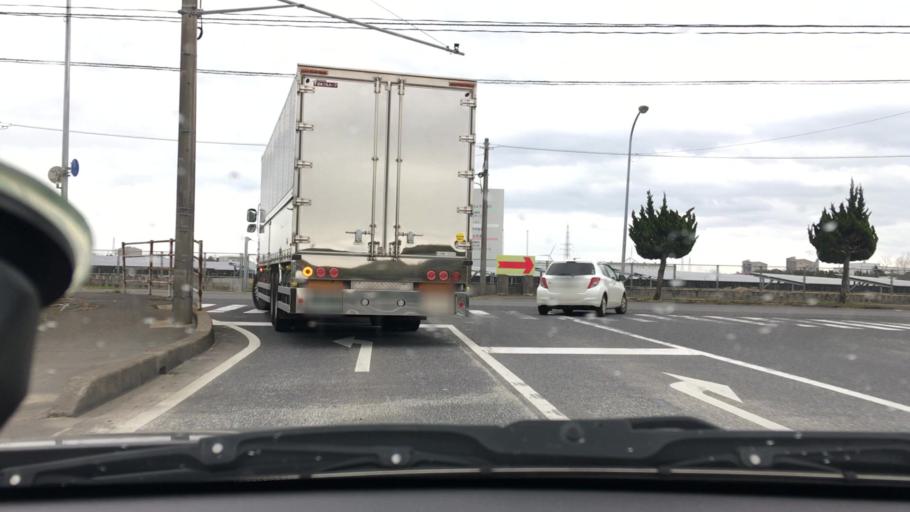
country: JP
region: Chiba
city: Omigawa
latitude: 35.8487
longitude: 140.7223
